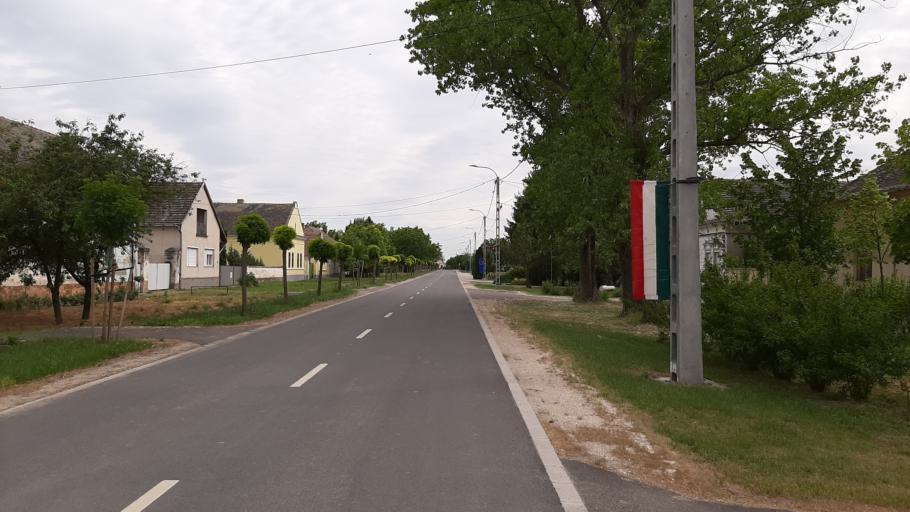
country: RO
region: Timis
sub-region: Comuna Beba Veche
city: Beba Veche
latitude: 46.1475
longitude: 20.2754
